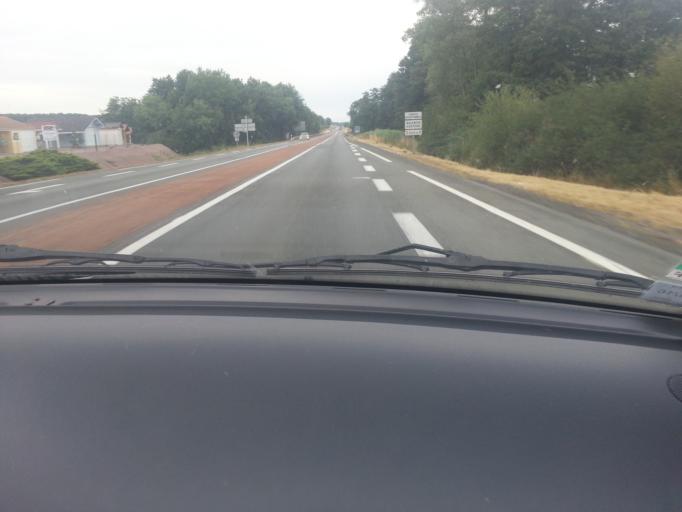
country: FR
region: Bourgogne
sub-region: Departement de Saone-et-Loire
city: Blanzy
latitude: 46.7027
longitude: 4.4135
